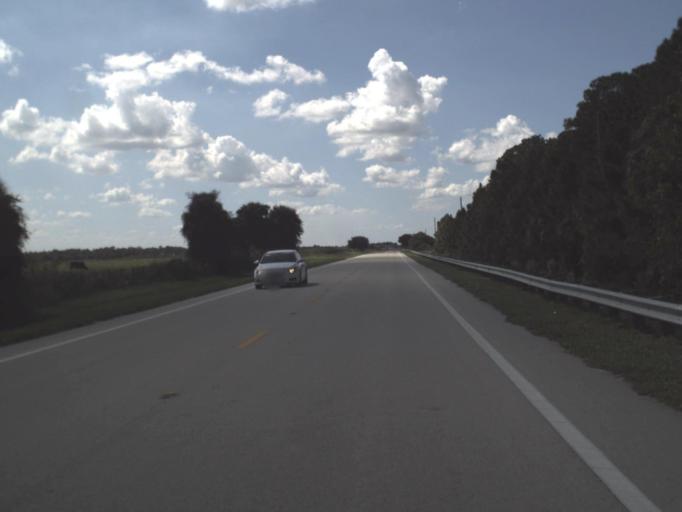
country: US
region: Florida
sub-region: Hendry County
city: Port LaBelle
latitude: 26.8125
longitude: -81.3695
